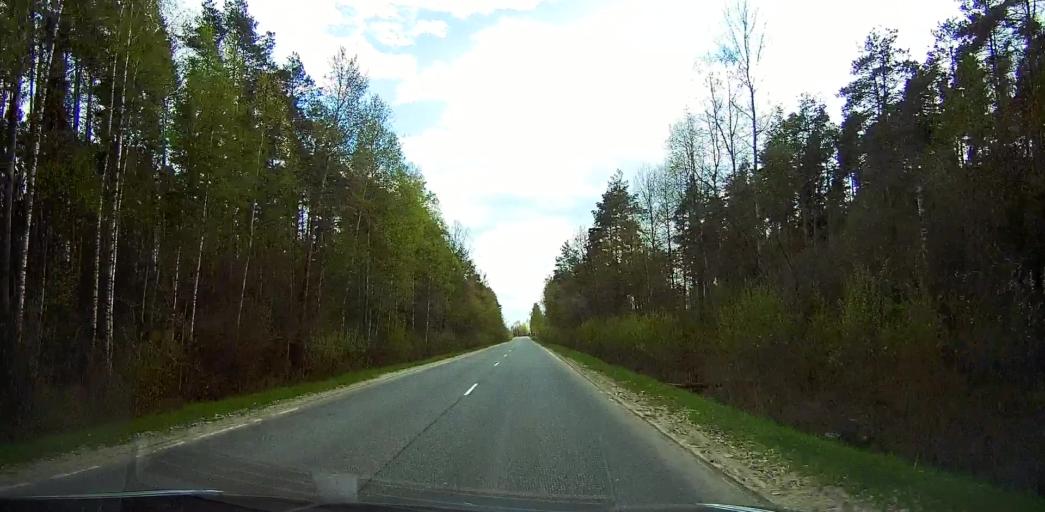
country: RU
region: Moskovskaya
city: Davydovo
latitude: 55.6519
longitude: 38.7548
